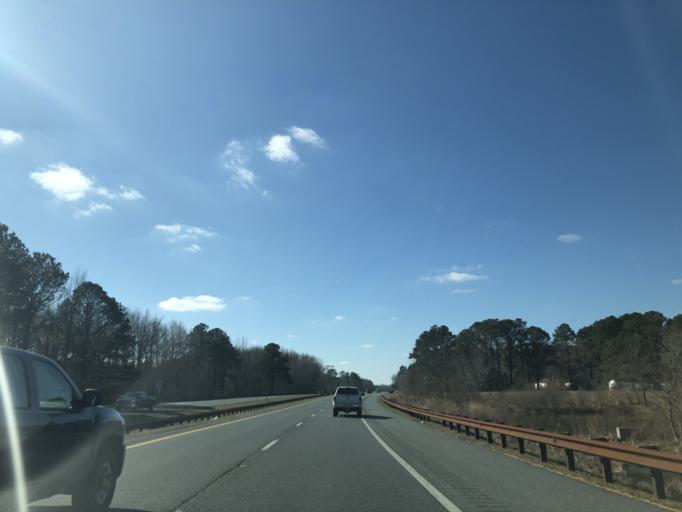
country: US
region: Maryland
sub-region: Worcester County
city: Berlin
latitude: 38.2823
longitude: -75.2326
